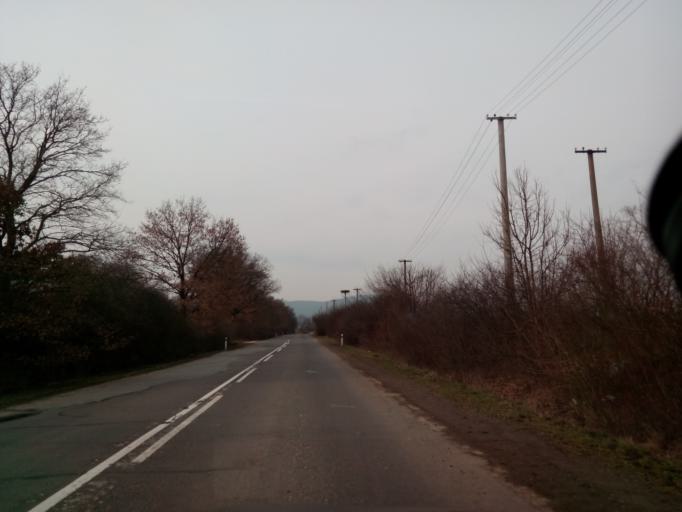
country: SK
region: Kosicky
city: Secovce
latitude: 48.6237
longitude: 21.5889
